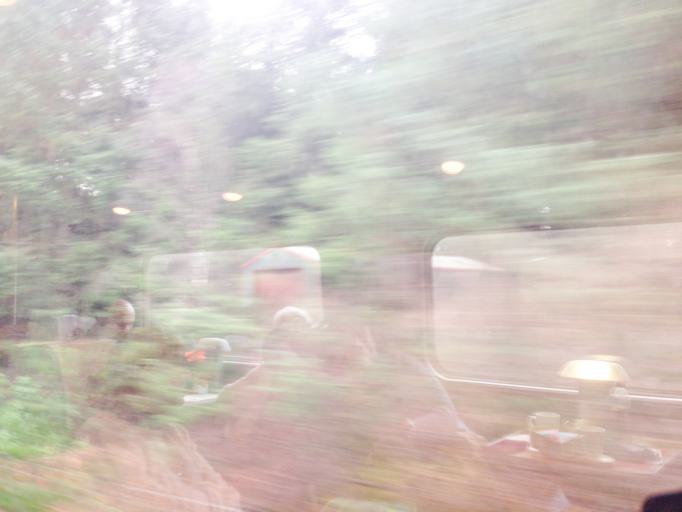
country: GB
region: Scotland
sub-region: Highland
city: Fort William
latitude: 56.8463
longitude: -5.1582
